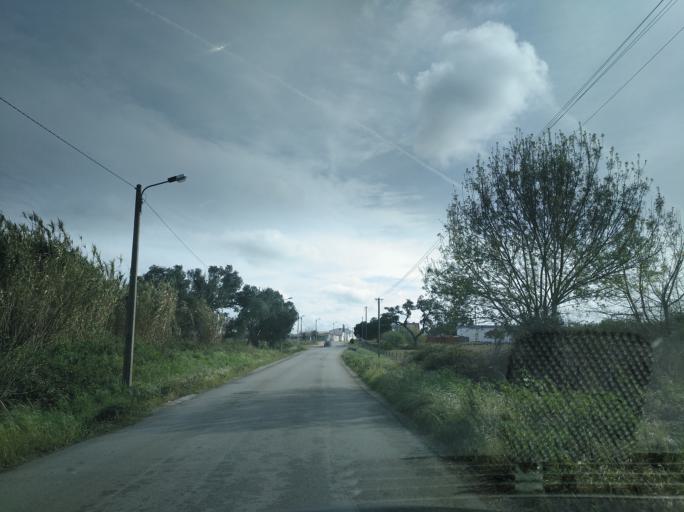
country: PT
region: Setubal
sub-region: Grandola
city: Grandola
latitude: 38.1856
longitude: -8.5564
